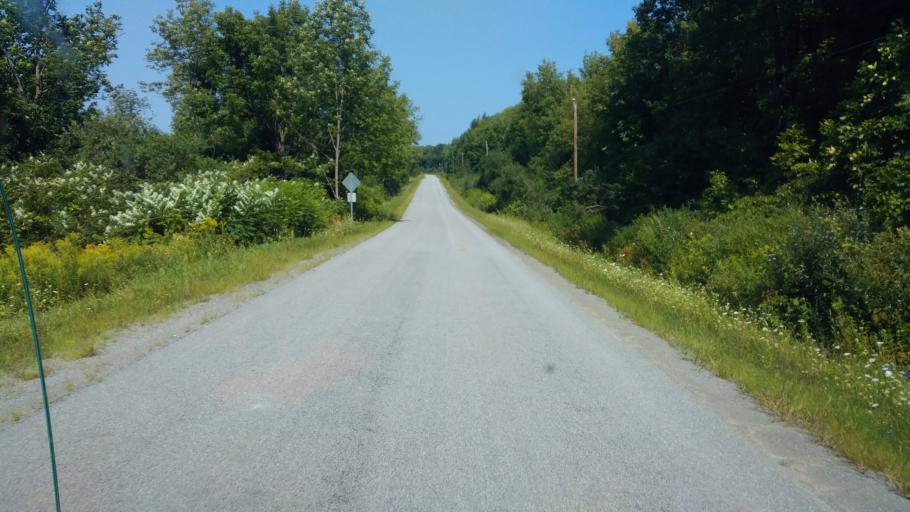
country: US
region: New York
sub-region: Allegany County
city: Belmont
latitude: 42.3156
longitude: -78.0677
